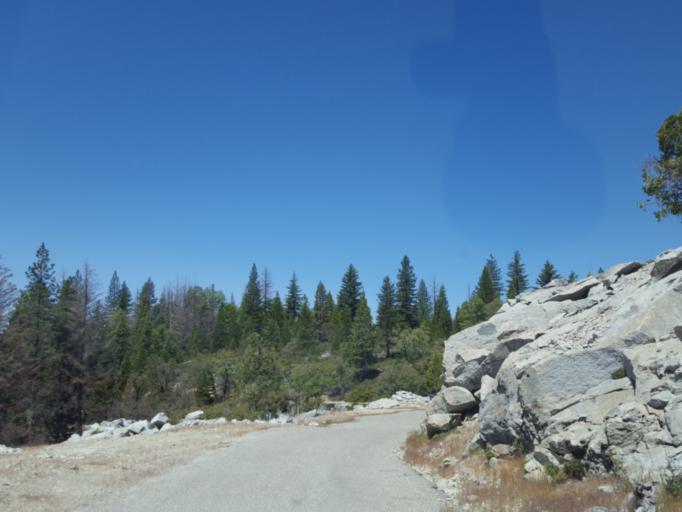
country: US
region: California
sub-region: Madera County
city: Oakhurst
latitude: 37.3535
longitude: -119.4840
